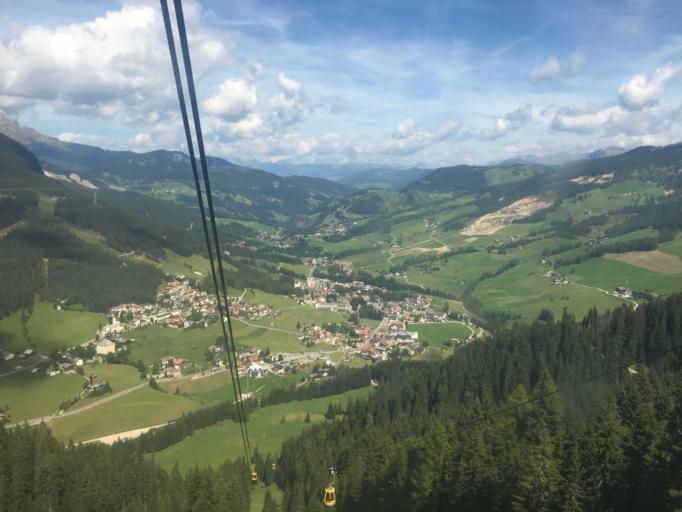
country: IT
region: Trentino-Alto Adige
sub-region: Bolzano
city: Corvara in Badia
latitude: 46.5713
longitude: 11.9041
